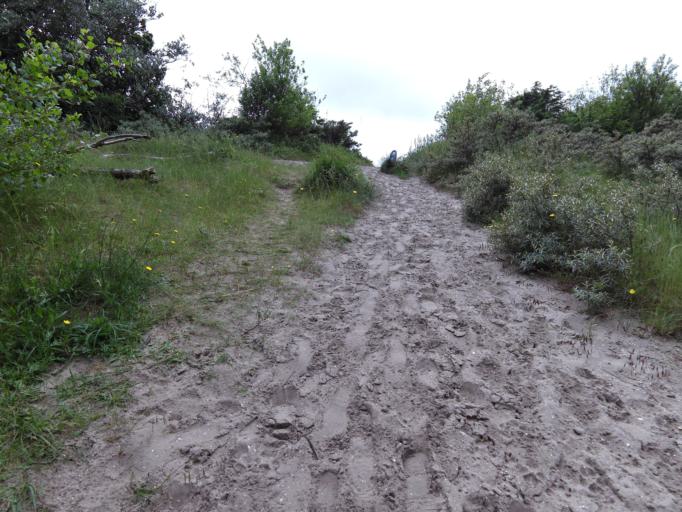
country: NL
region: South Holland
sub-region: Gemeente Hellevoetsluis
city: Nieuw-Helvoet
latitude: 51.8685
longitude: 4.0534
